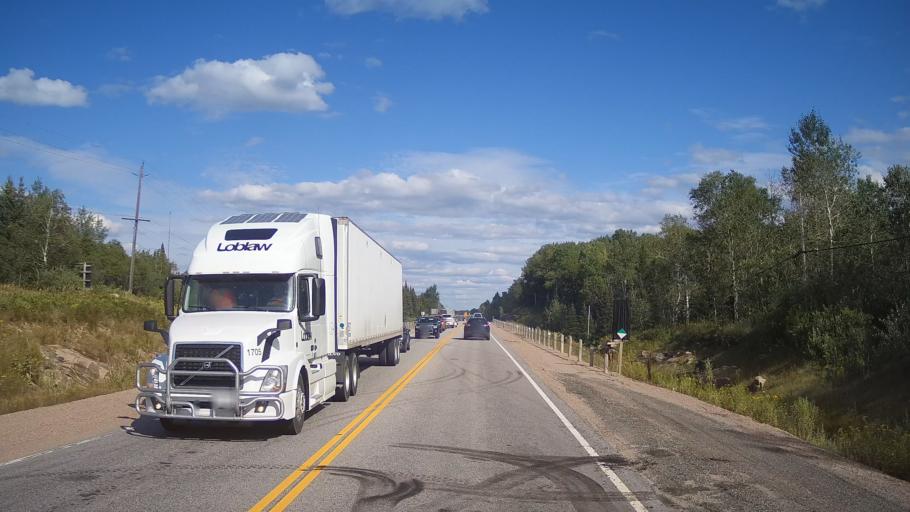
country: CA
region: Ontario
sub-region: Nipissing District
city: North Bay
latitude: 46.2798
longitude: -79.2958
